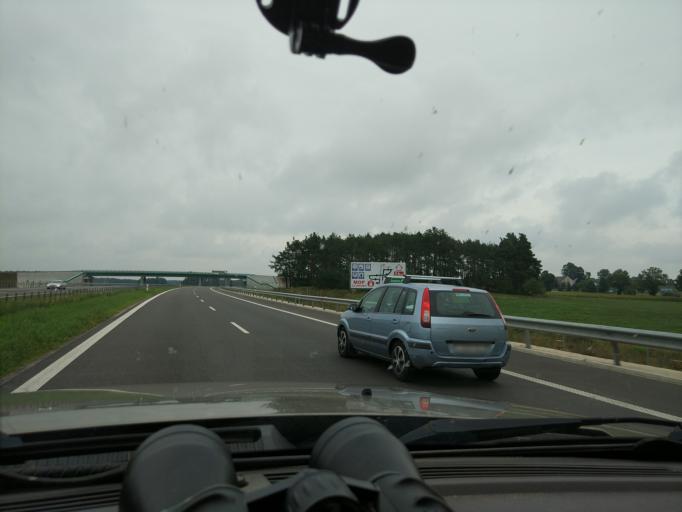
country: PL
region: Podlasie
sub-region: Powiat zambrowski
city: Szumowo
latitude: 52.8872
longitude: 22.0494
